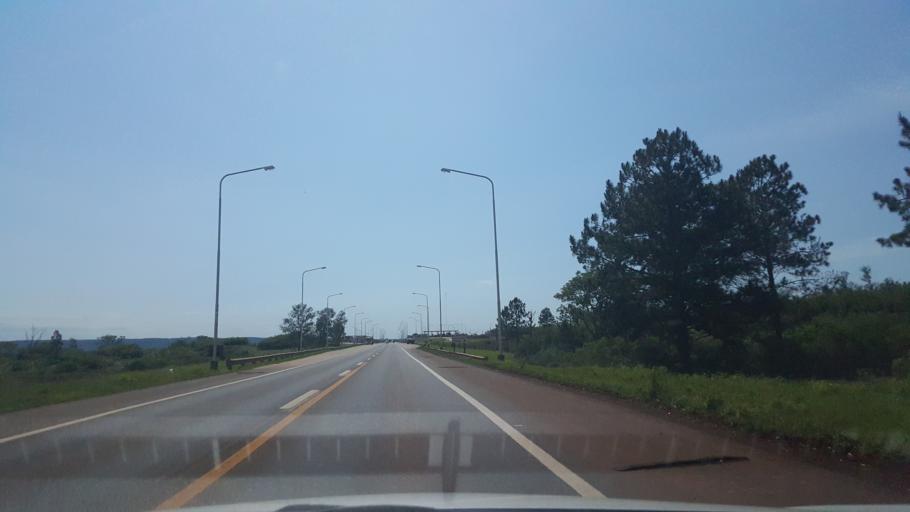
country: AR
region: Misiones
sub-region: Departamento de Apostoles
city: San Jose
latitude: -27.7849
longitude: -55.8241
